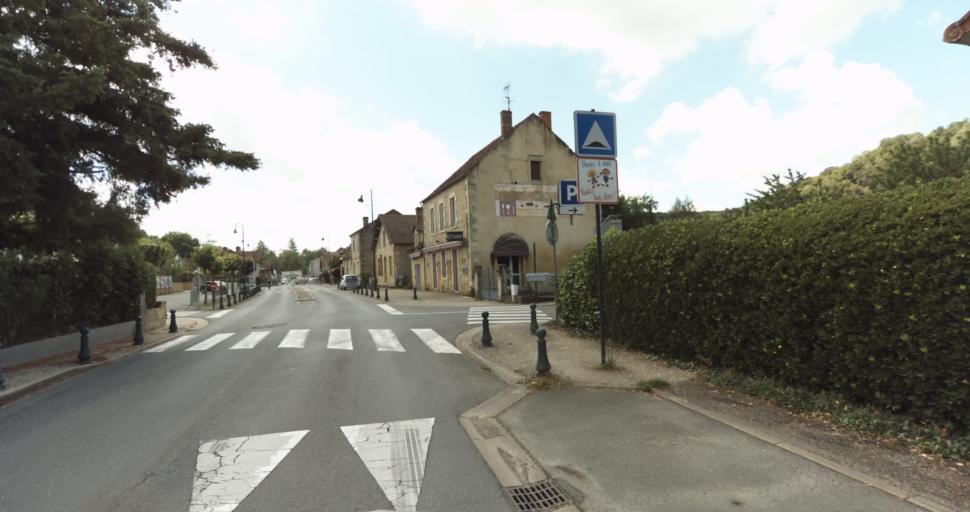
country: FR
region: Aquitaine
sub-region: Departement de la Dordogne
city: Lalinde
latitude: 44.8295
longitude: 0.7038
